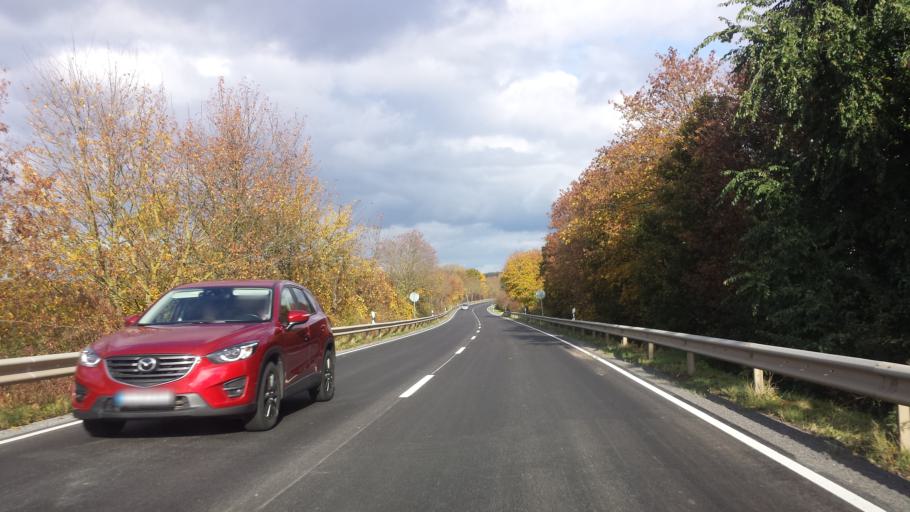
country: DE
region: Rheinland-Pfalz
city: Schifferstadt
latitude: 49.3985
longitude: 8.3602
